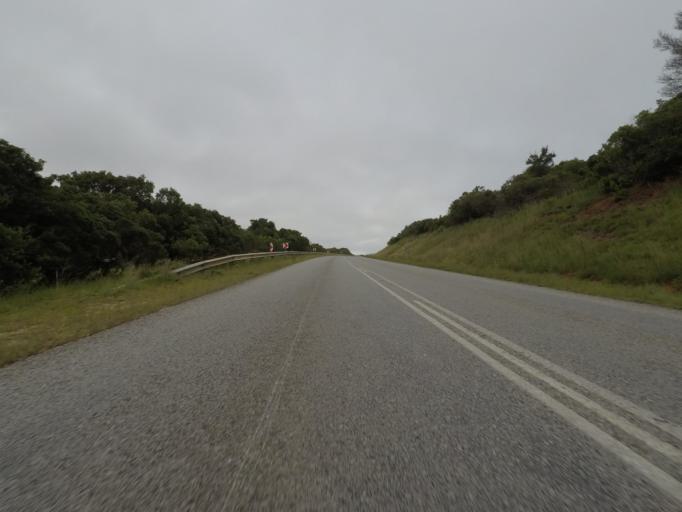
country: ZA
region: Eastern Cape
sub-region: Cacadu District Municipality
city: Port Alfred
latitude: -33.6116
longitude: 26.8067
